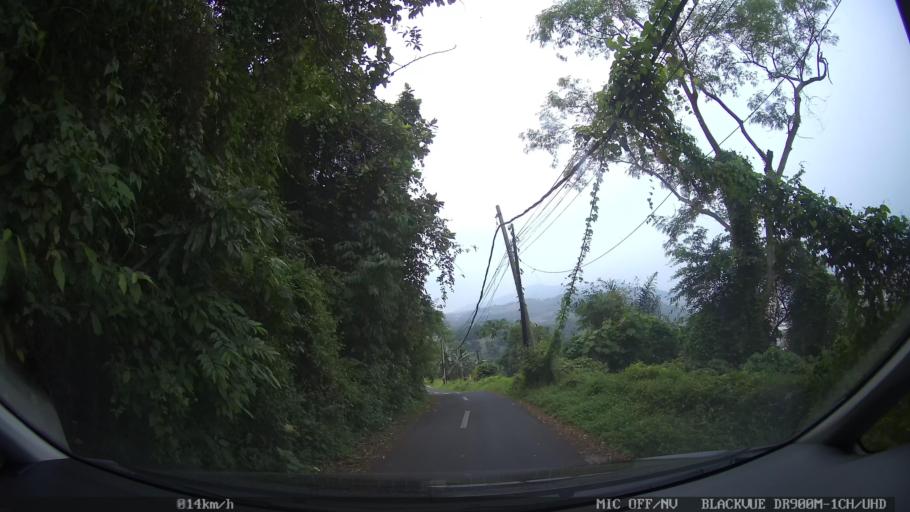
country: ID
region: Lampung
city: Panjang
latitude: -5.4362
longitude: 105.3103
